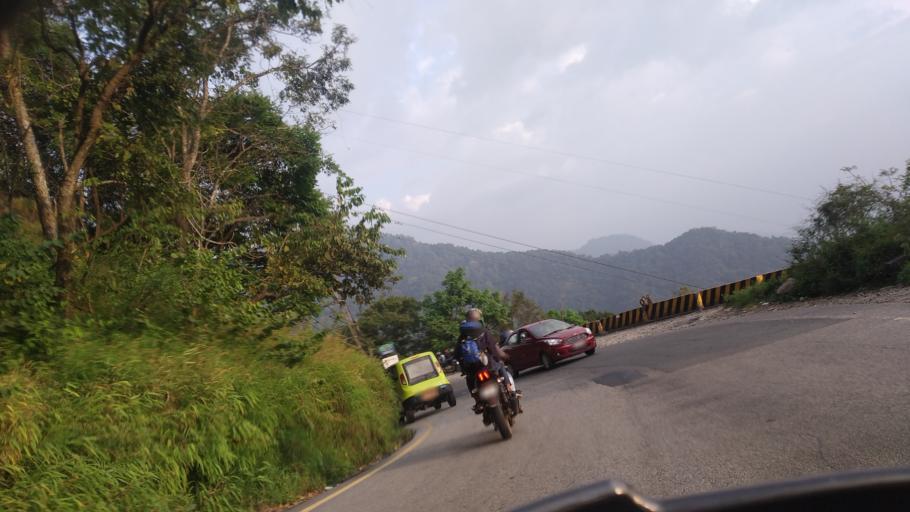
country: IN
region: Kerala
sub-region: Wayanad
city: Kalpetta
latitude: 11.5101
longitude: 76.0188
